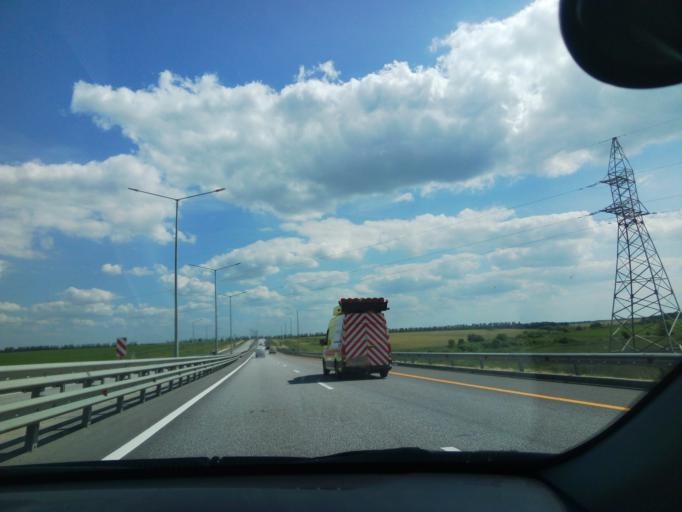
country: RU
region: Voronezj
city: Kashirskoye
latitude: 51.4941
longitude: 39.5276
